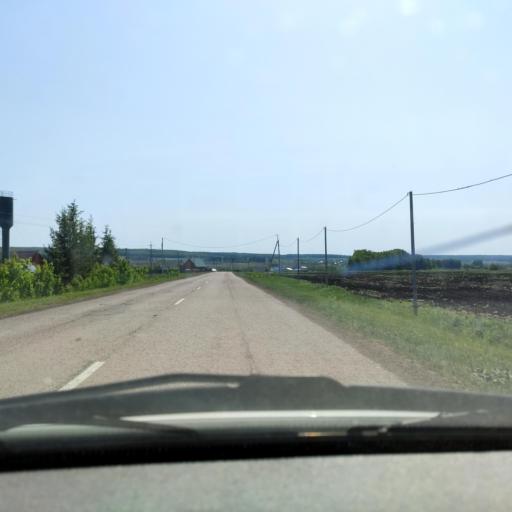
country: RU
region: Bashkortostan
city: Avdon
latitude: 54.5015
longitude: 55.6188
